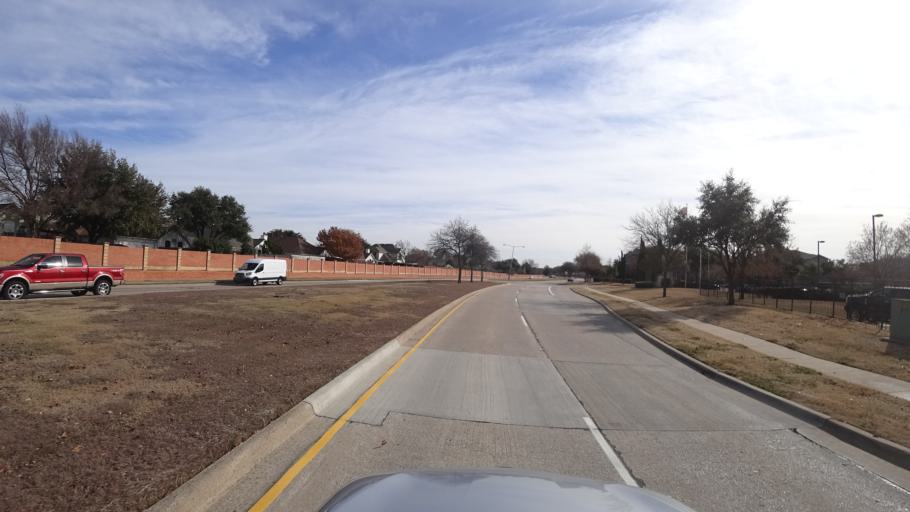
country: US
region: Texas
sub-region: Denton County
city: Highland Village
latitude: 33.0613
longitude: -97.0309
